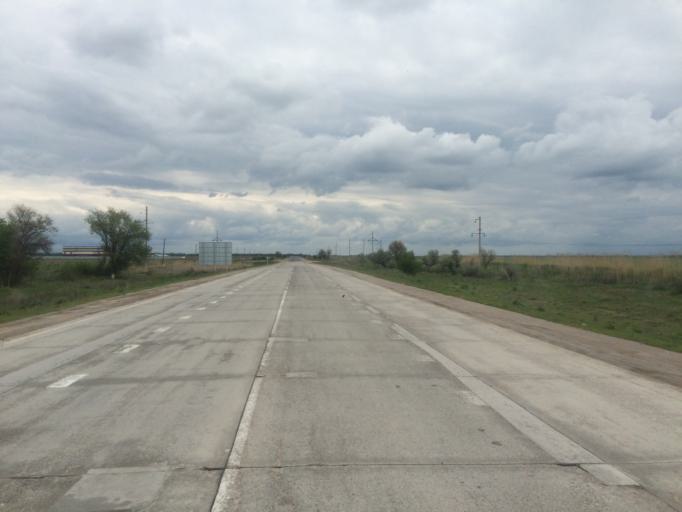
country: KG
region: Chuy
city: Sokuluk
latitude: 43.2706
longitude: 74.2417
